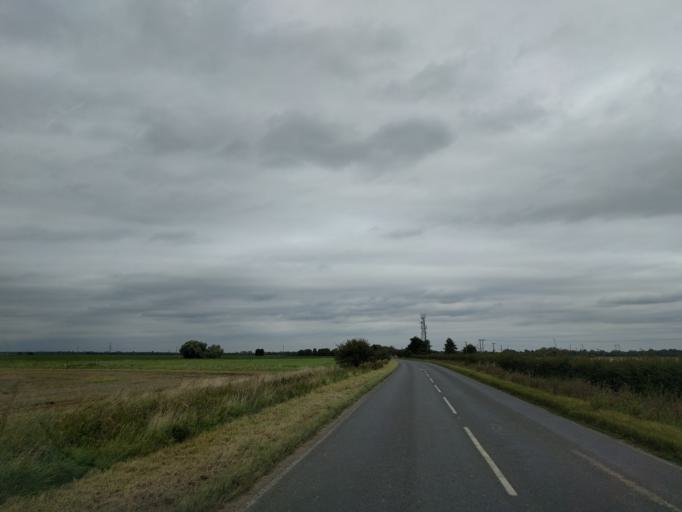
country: GB
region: England
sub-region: Cambridgeshire
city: Swavesey
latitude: 52.2637
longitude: 0.0298
